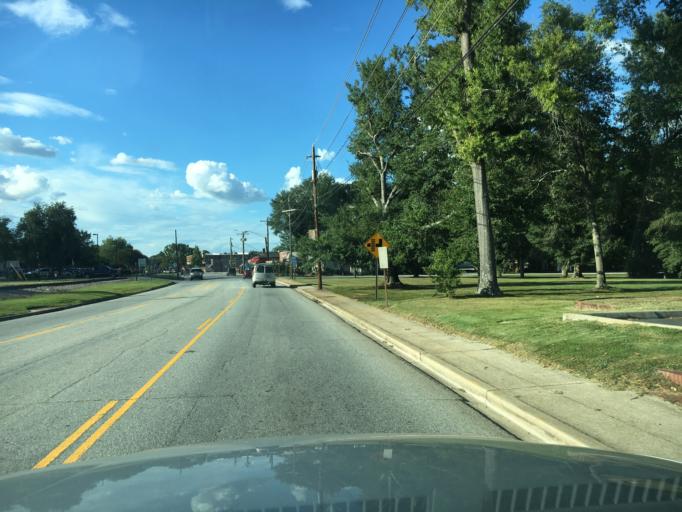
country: US
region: South Carolina
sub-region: Greenville County
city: Simpsonville
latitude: 34.7348
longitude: -82.2545
